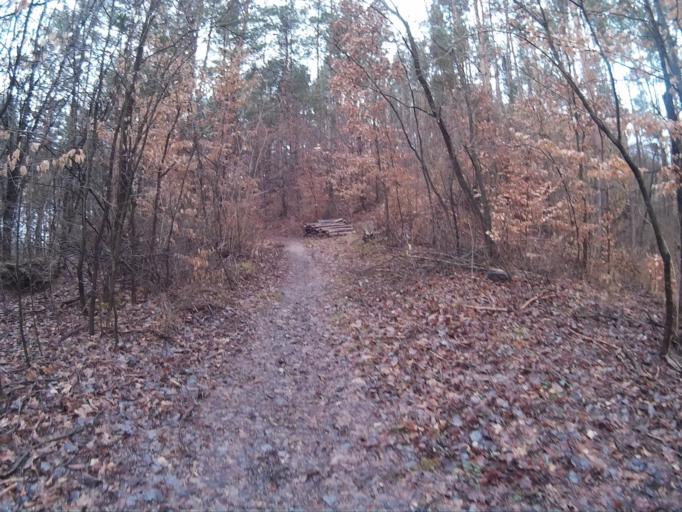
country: HU
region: Borsod-Abauj-Zemplen
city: Sarospatak
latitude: 48.4712
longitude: 21.4700
